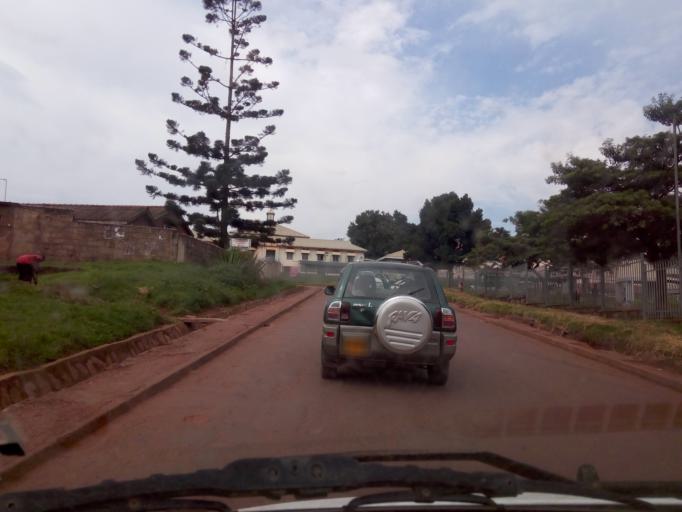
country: UG
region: Central Region
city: Kampala Central Division
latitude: 0.3412
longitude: 32.5759
